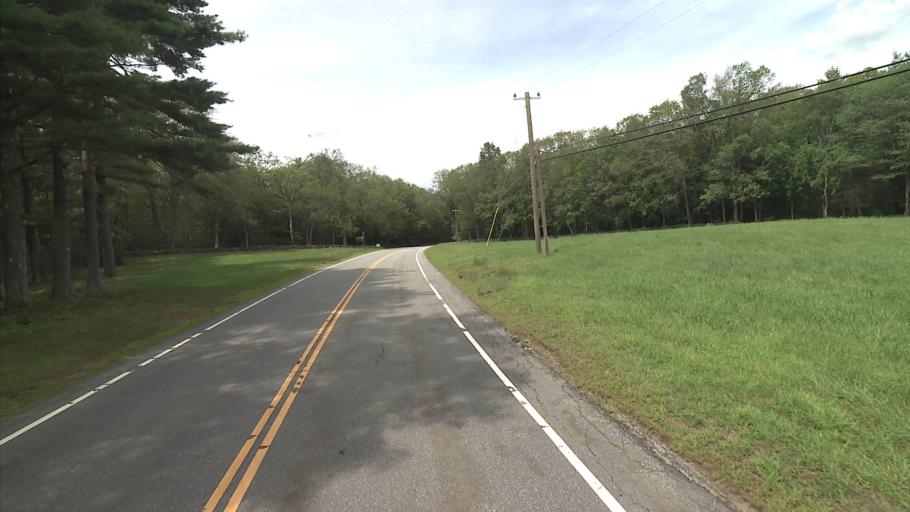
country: US
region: Massachusetts
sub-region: Hampden County
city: Holland
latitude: 41.9409
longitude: -72.1024
